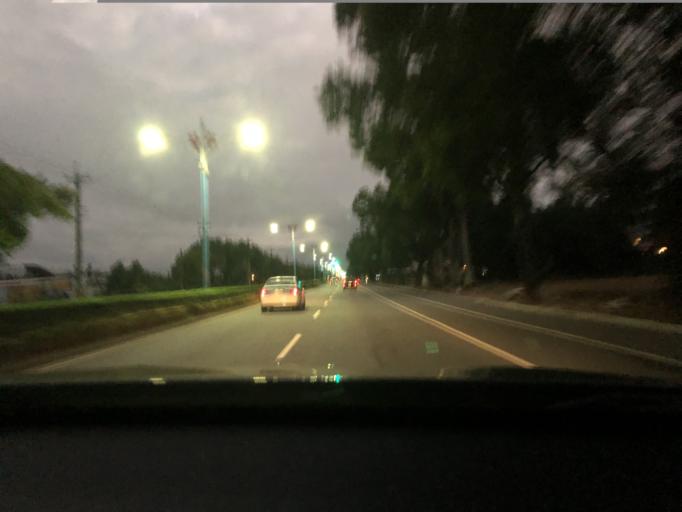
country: TW
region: Taiwan
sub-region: Hualien
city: Hualian
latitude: 23.9611
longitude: 121.5647
